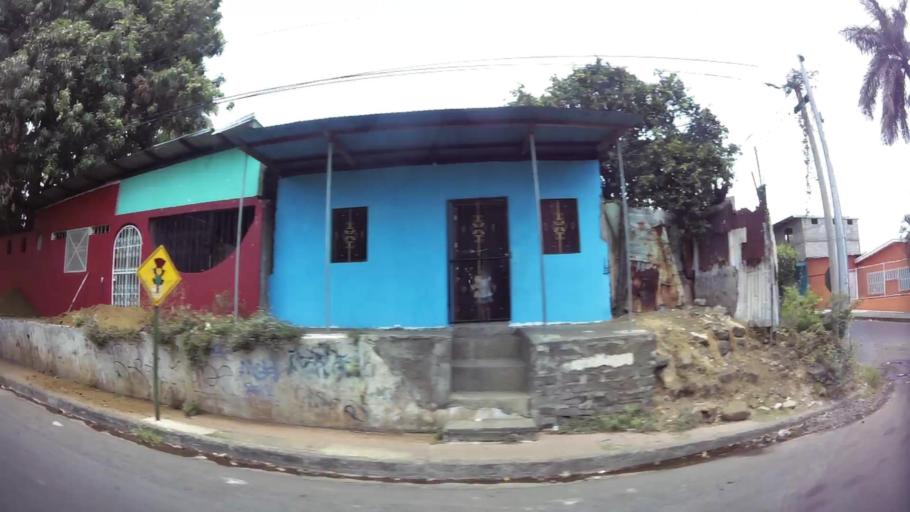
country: NI
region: Managua
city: Managua
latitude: 12.1388
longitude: -86.2916
